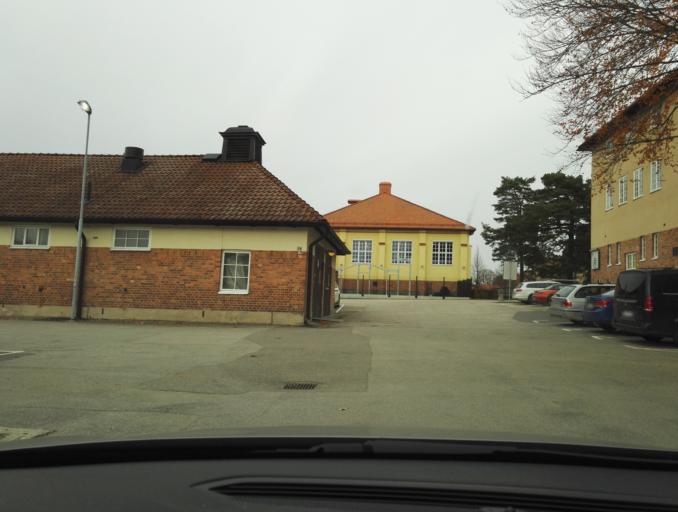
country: SE
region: Kronoberg
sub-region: Vaxjo Kommun
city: Vaexjoe
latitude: 56.8764
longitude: 14.7794
